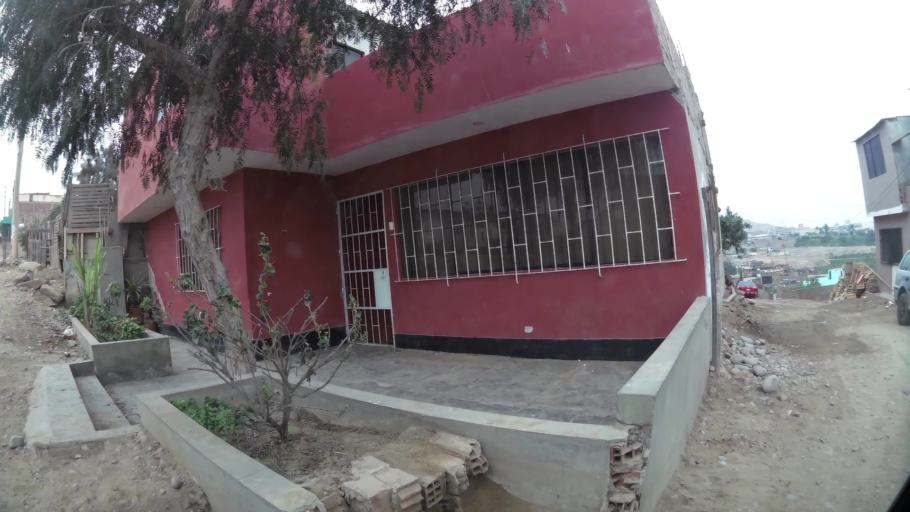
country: PE
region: Lima
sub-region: Lima
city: Surco
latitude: -12.2059
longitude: -76.9801
